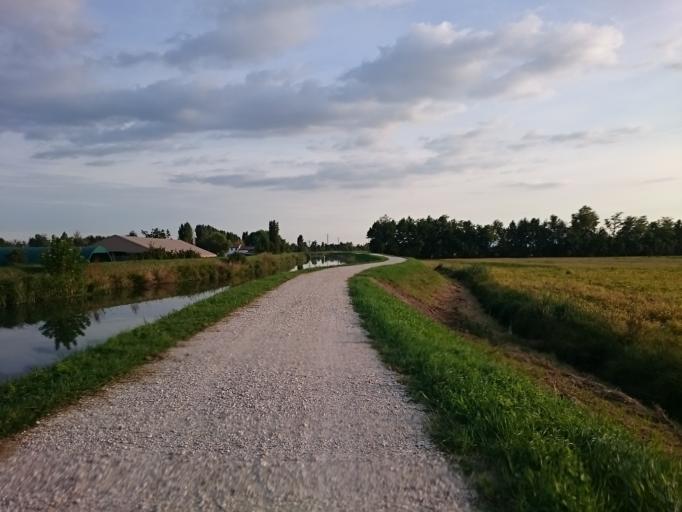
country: IT
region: Veneto
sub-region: Provincia di Padova
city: Campodoro
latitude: 45.4996
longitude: 11.7339
